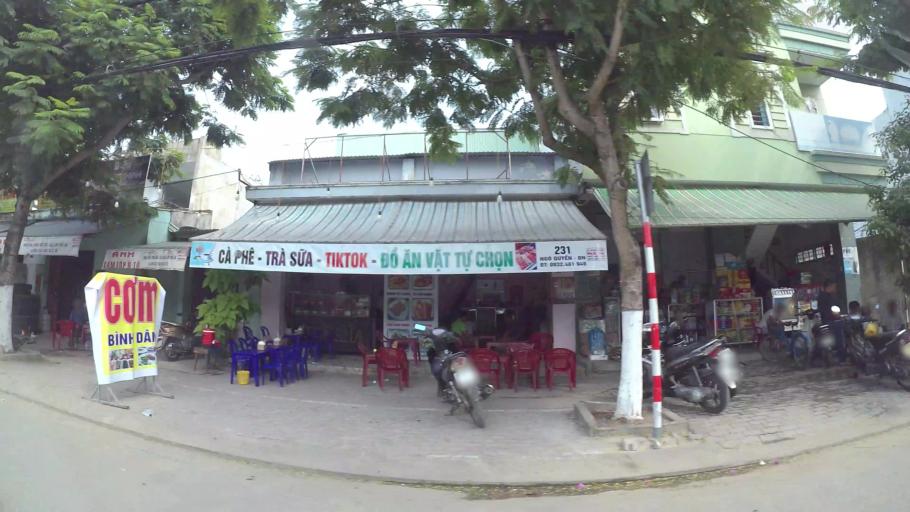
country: VN
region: Da Nang
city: Son Tra
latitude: 16.0905
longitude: 108.2429
